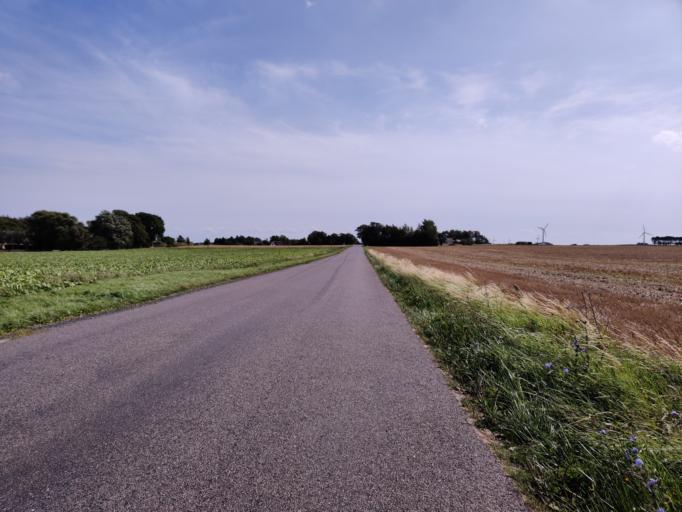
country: DK
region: Zealand
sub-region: Guldborgsund Kommune
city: Nykobing Falster
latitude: 54.6268
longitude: 11.9084
